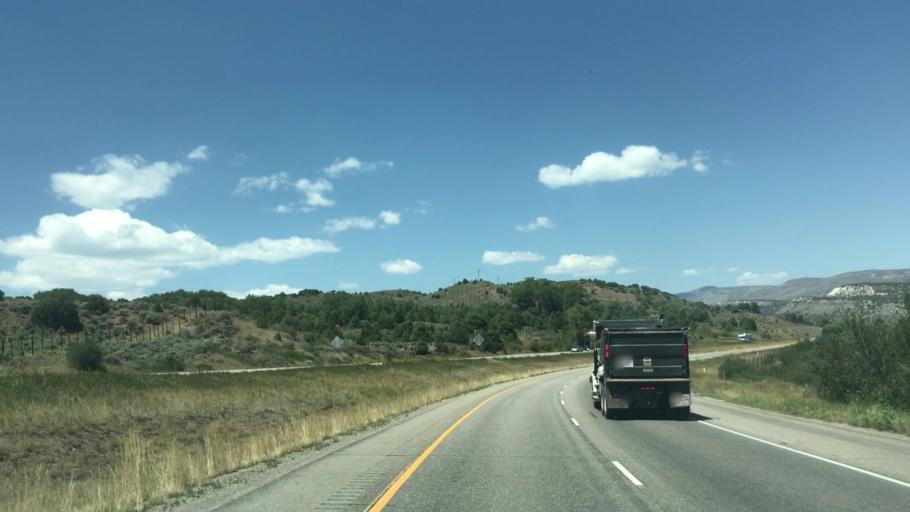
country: US
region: Colorado
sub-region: Eagle County
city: Edwards
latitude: 39.6837
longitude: -106.6588
